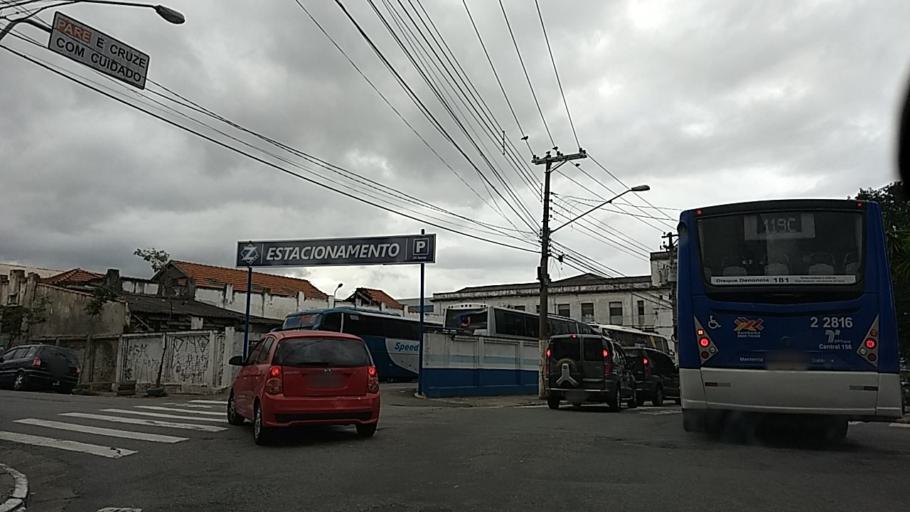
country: BR
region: Sao Paulo
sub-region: Sao Paulo
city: Sao Paulo
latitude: -23.5287
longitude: -46.6157
